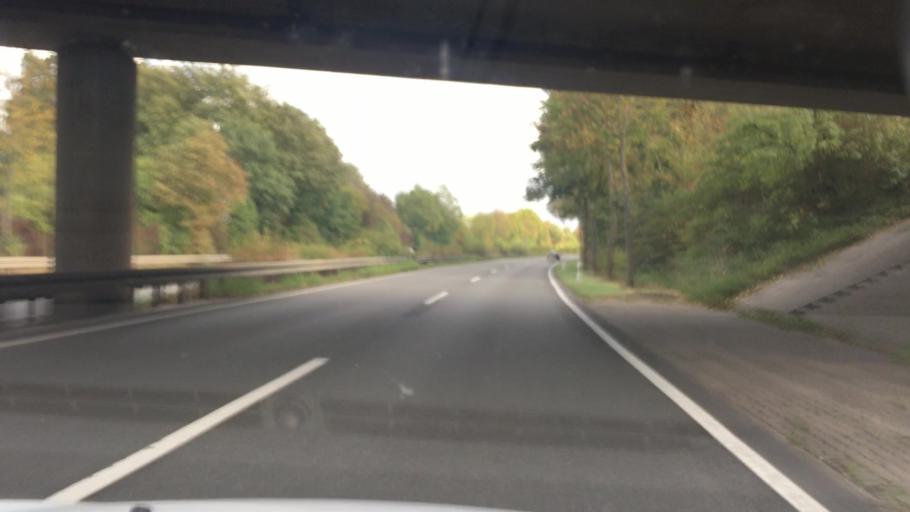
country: DE
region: Lower Saxony
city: Garbsen
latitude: 52.4647
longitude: 9.5324
